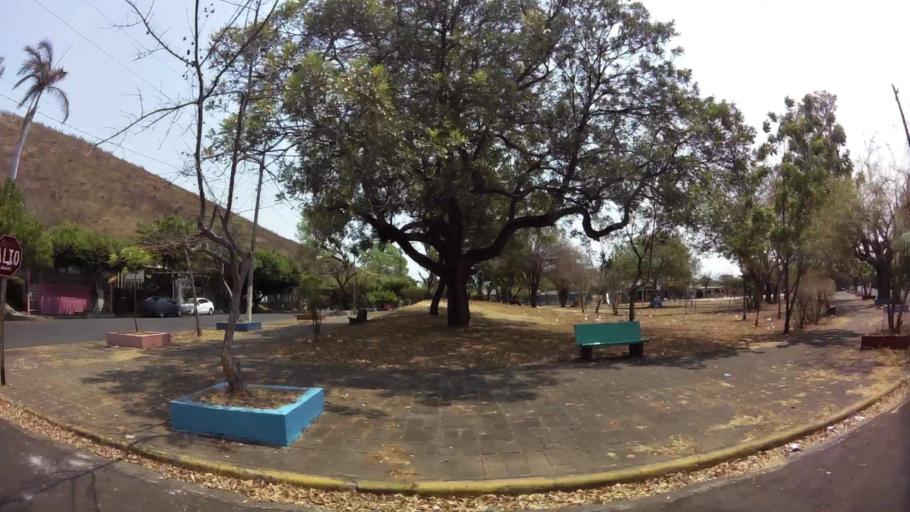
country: NI
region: Managua
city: Ciudad Sandino
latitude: 12.1514
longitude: -86.3160
